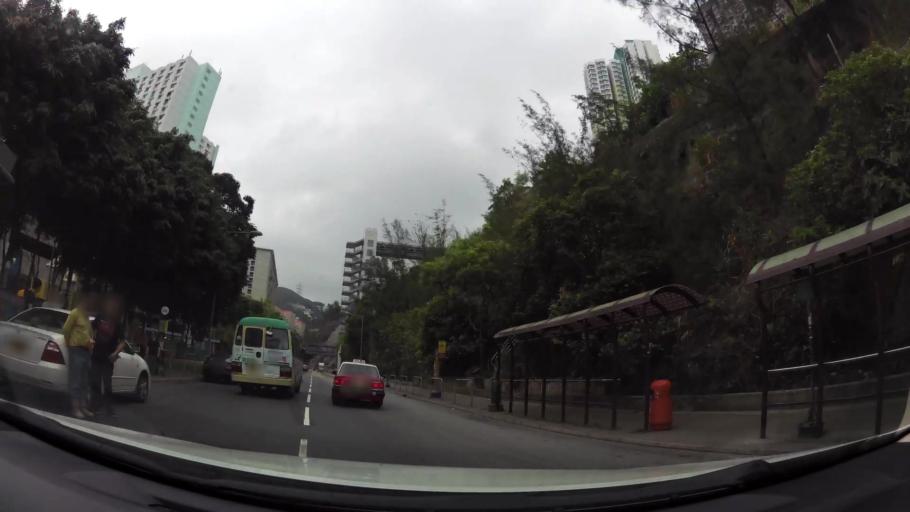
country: HK
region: Kowloon City
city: Kowloon
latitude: 22.3280
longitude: 114.2269
